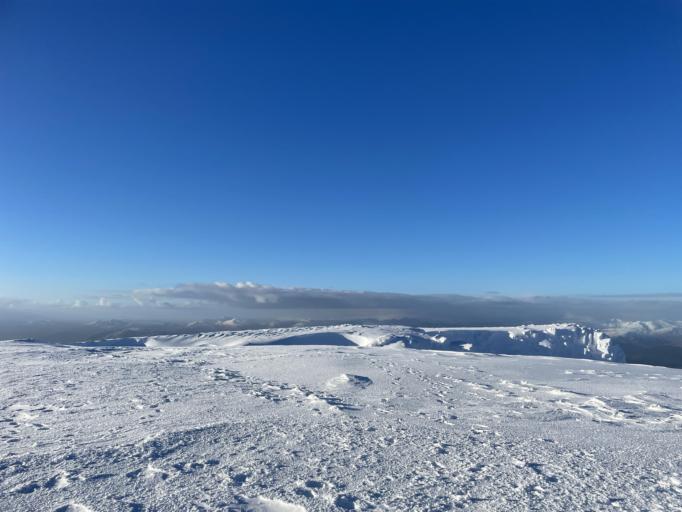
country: GB
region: Scotland
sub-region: Highland
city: Fort William
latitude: 56.7965
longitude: -5.0042
